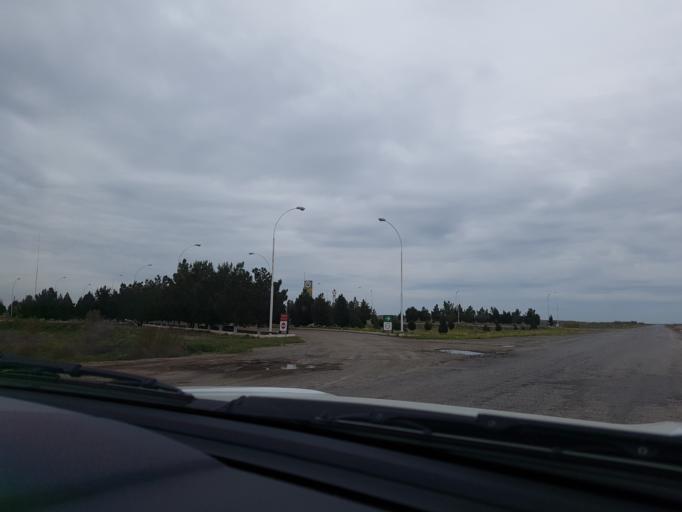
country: TM
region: Mary
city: Bayramaly
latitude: 37.9628
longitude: 62.6620
